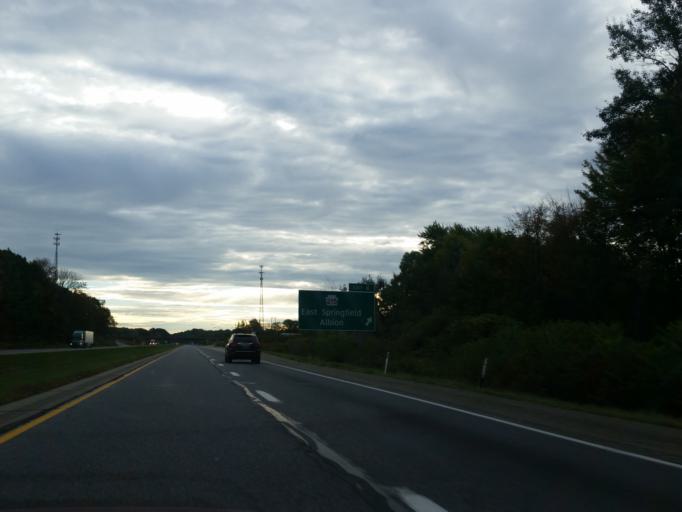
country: US
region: Pennsylvania
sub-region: Erie County
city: Albion
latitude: 41.9445
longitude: -80.4095
